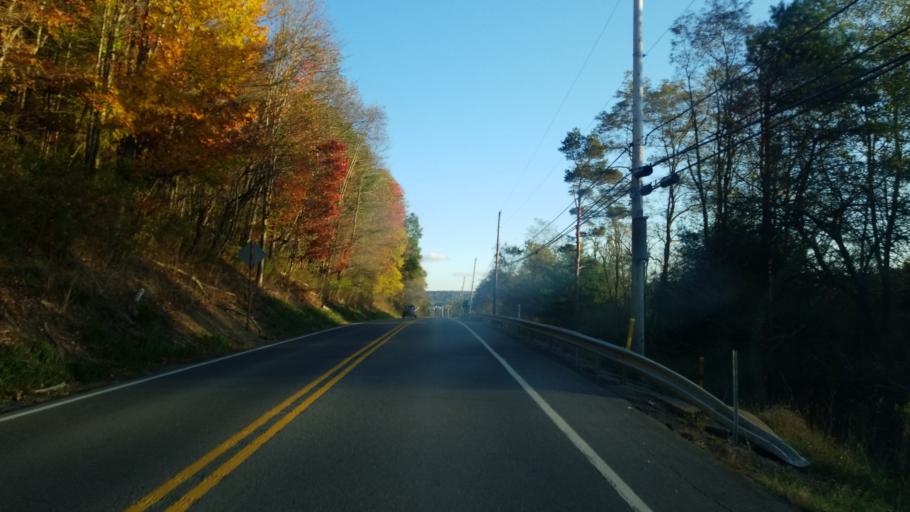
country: US
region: Pennsylvania
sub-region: Jefferson County
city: Punxsutawney
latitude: 40.9627
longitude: -78.9679
